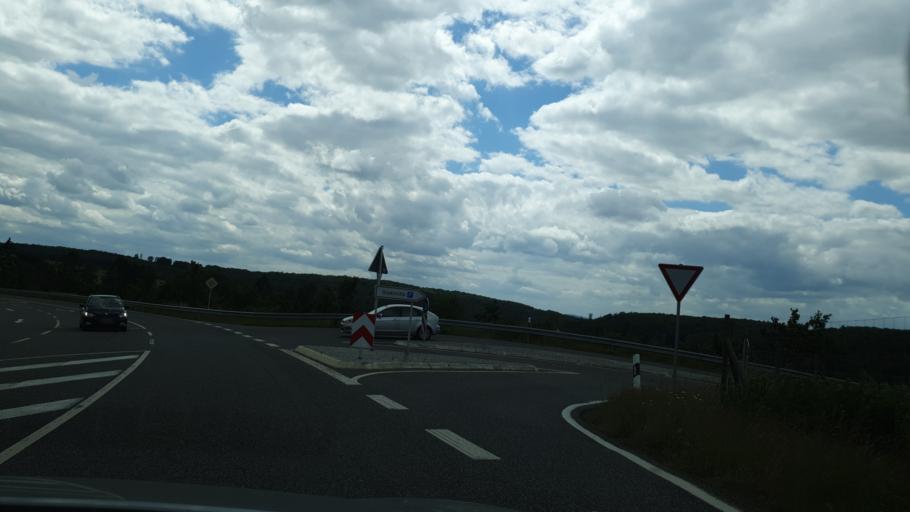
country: DE
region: Rheinland-Pfalz
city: Hohr-Grenzhausen
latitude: 50.4244
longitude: 7.6817
